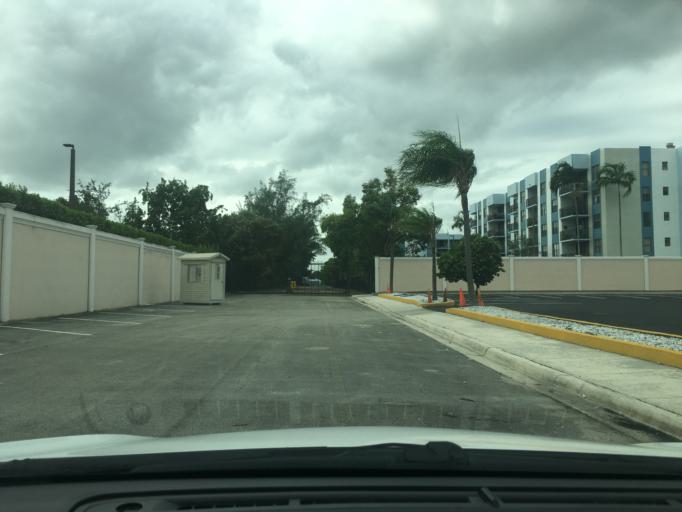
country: US
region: Florida
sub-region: Miami-Dade County
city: Biscayne Park
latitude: 25.8875
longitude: -80.1667
